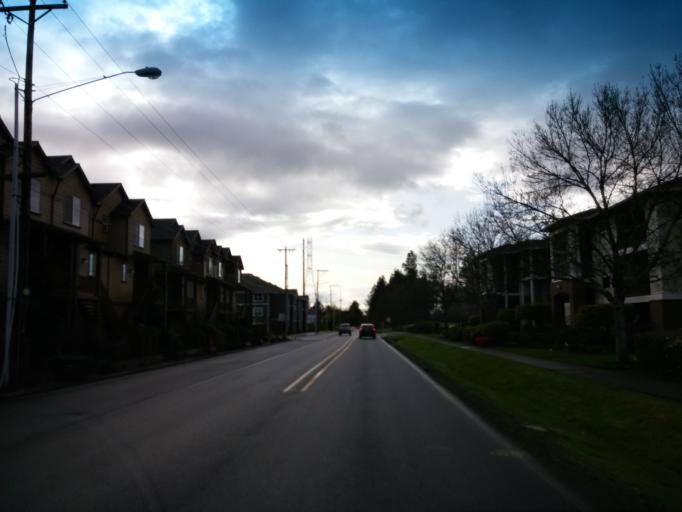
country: US
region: Oregon
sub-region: Washington County
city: Oak Hills
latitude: 45.5126
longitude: -122.8433
